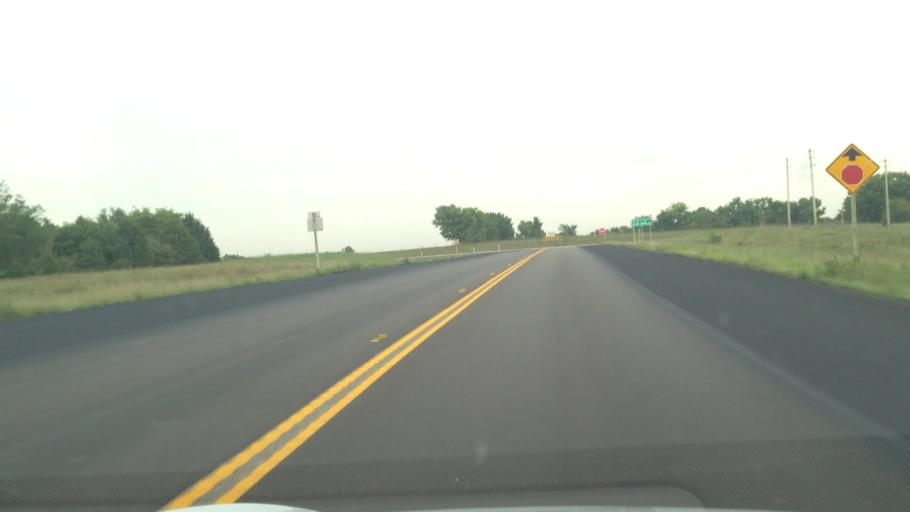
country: US
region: Kansas
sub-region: Cherokee County
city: Baxter Springs
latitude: 37.0255
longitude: -94.7020
